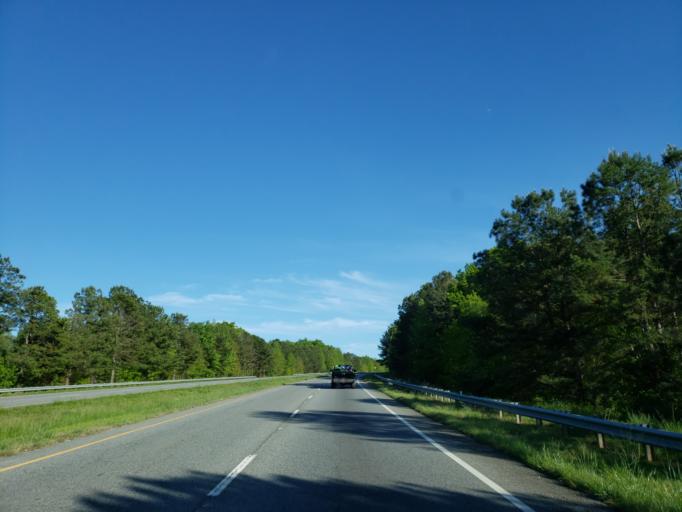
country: US
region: Georgia
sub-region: Polk County
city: Rockmart
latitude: 33.9634
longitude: -84.9907
